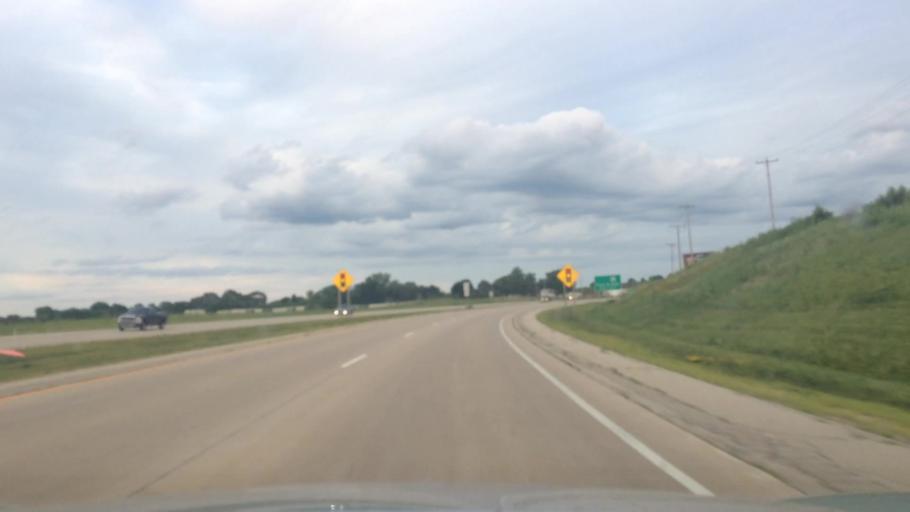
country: US
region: Wisconsin
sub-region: Dane County
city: Waunakee
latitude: 43.1899
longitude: -89.5596
